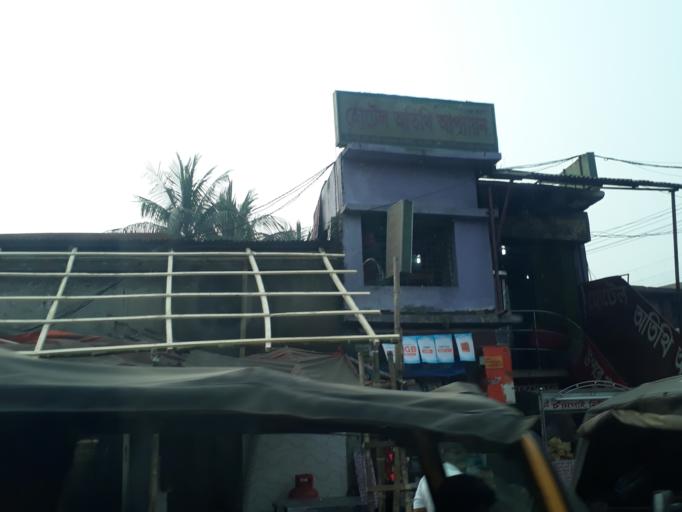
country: BD
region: Khulna
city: Khulna
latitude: 22.8975
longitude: 89.5100
